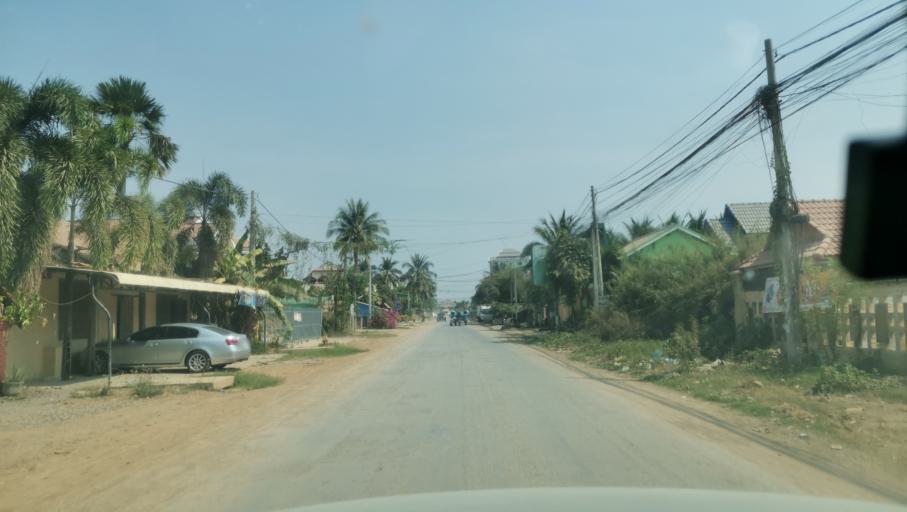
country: KH
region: Battambang
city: Battambang
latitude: 13.0984
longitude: 103.2053
